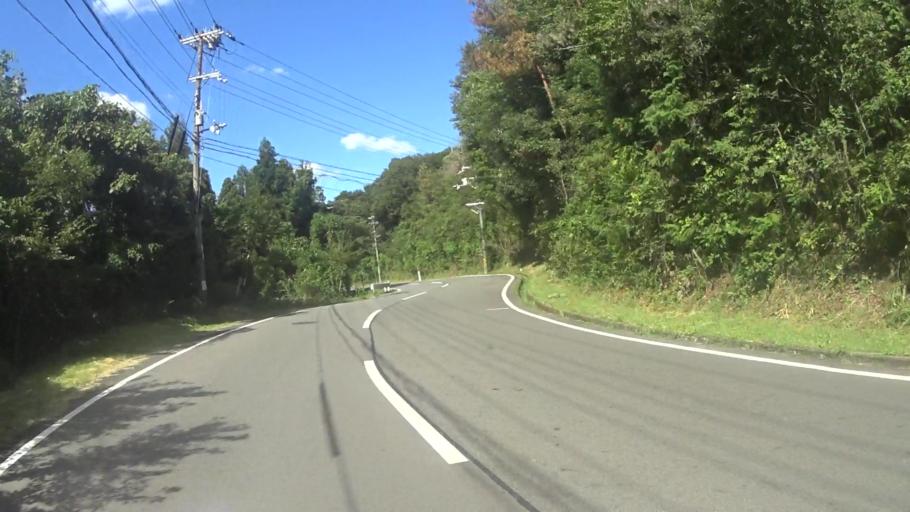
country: JP
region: Mie
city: Ueno-ebisumachi
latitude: 34.7451
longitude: 136.0226
